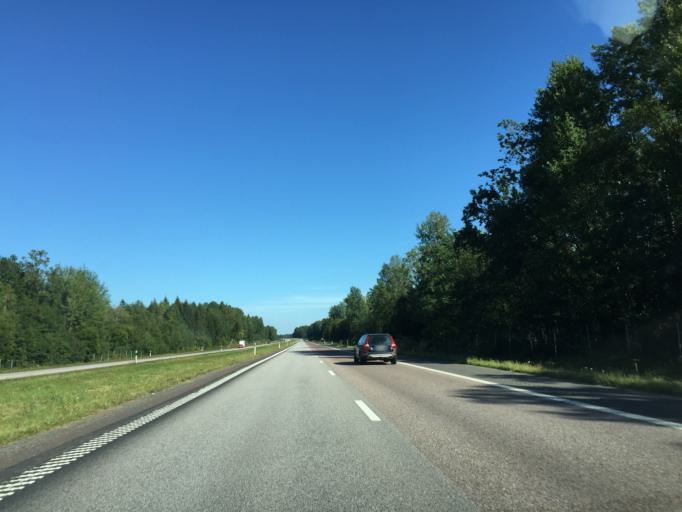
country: SE
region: OErebro
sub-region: Orebro Kommun
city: Hovsta
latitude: 59.3070
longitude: 15.2998
